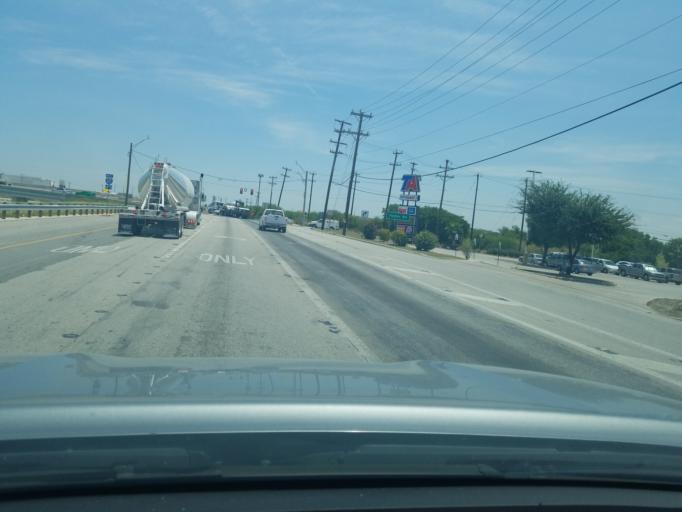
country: US
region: Texas
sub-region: Bexar County
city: Kirby
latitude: 29.4442
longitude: -98.3620
